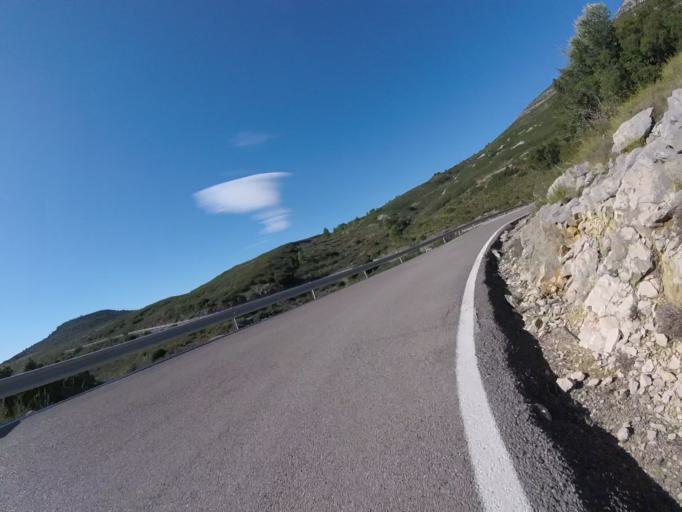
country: ES
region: Valencia
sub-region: Provincia de Castello
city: Albocasser
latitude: 40.3945
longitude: 0.0405
